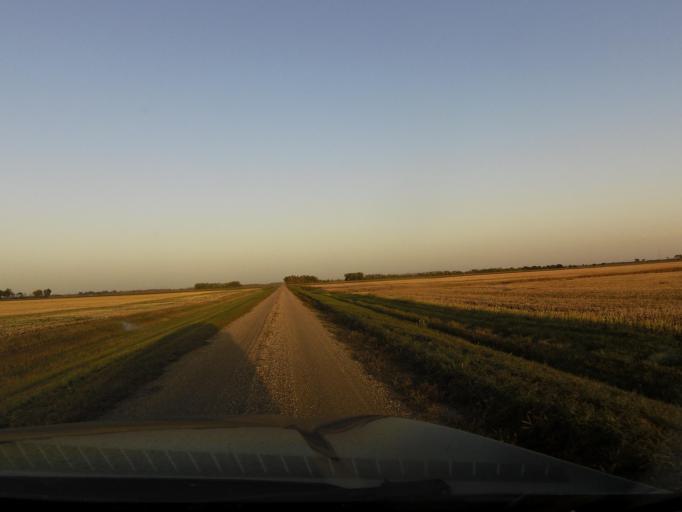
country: US
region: North Dakota
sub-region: Walsh County
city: Grafton
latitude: 48.3831
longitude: -97.2185
